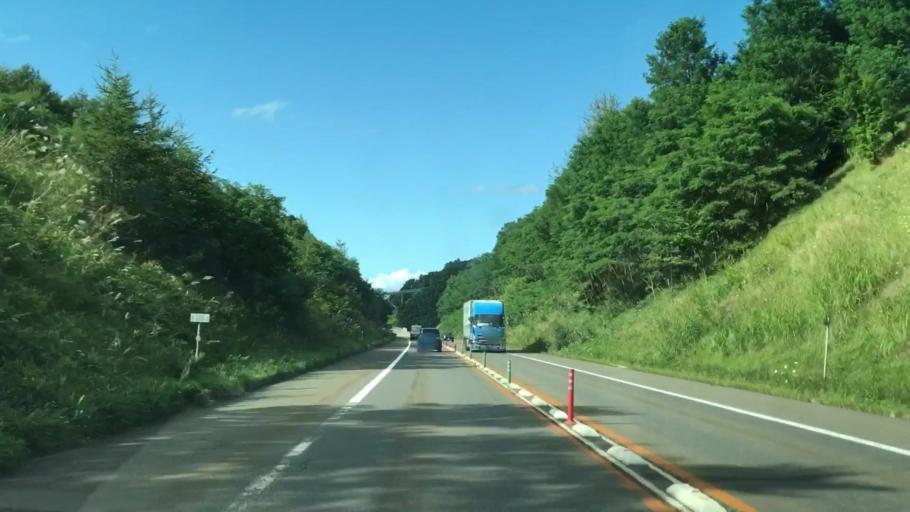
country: JP
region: Hokkaido
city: Date
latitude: 42.4556
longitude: 140.9127
